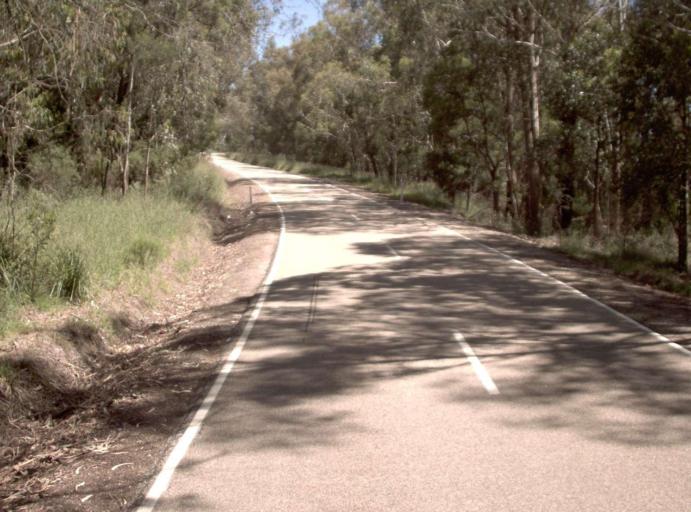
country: AU
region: Victoria
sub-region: East Gippsland
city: Lakes Entrance
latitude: -37.2636
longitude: 148.2502
